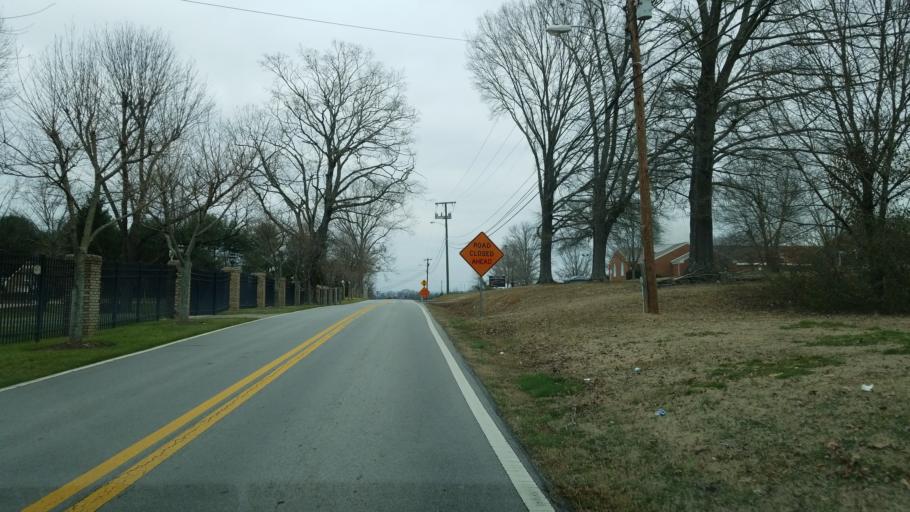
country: US
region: Tennessee
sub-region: Hamilton County
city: East Brainerd
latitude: 35.0555
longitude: -85.1585
